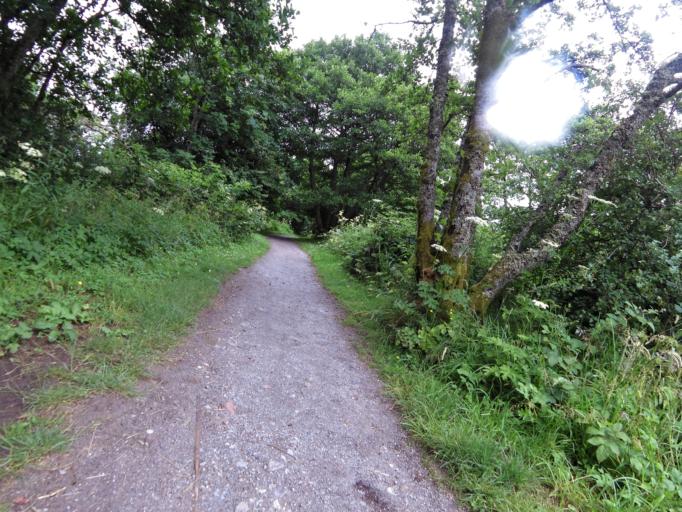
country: GB
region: Scotland
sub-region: Highland
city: Fort William
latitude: 56.8286
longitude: -5.0939
